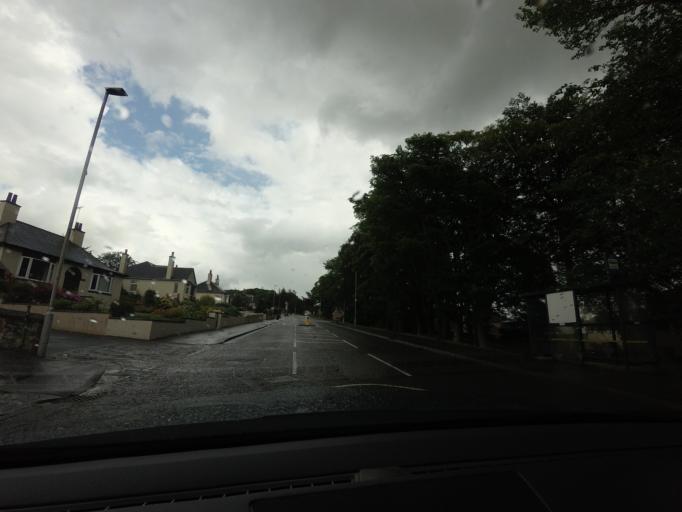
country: GB
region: Scotland
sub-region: Aberdeenshire
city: Turriff
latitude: 57.5398
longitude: -2.4555
